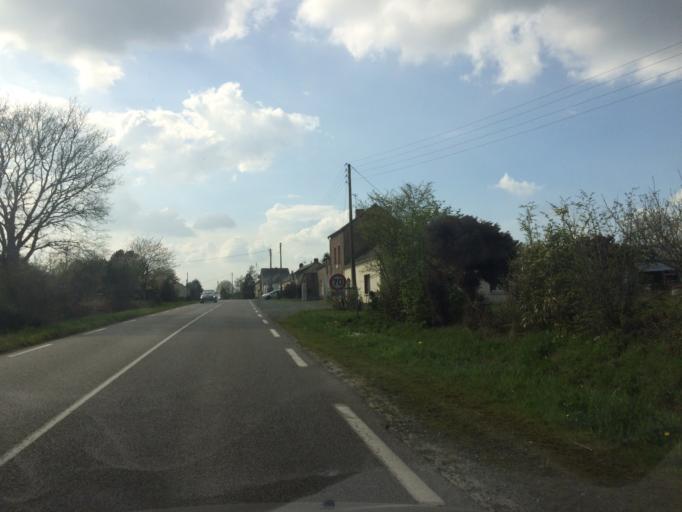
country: FR
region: Pays de la Loire
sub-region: Departement de la Loire-Atlantique
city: Blain
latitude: 47.4815
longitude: -1.7915
